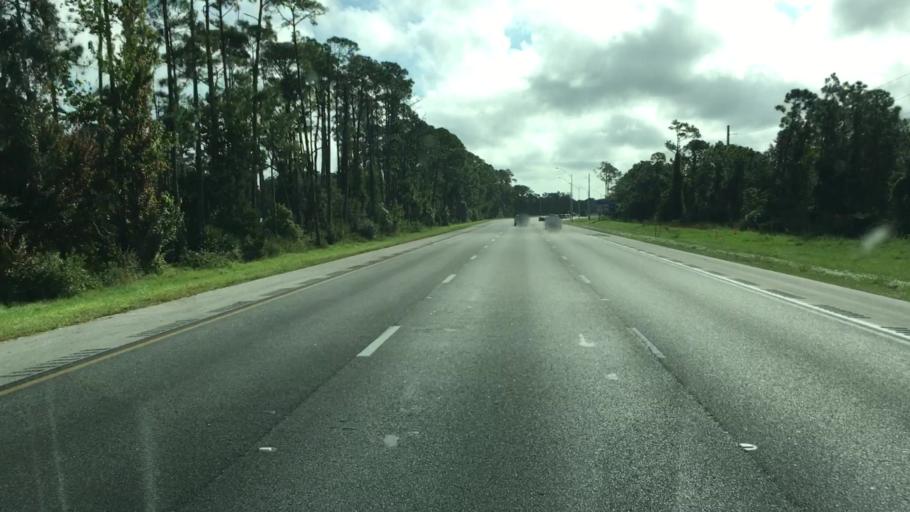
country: US
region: Florida
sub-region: Volusia County
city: Port Orange
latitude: 29.1152
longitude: -81.0364
